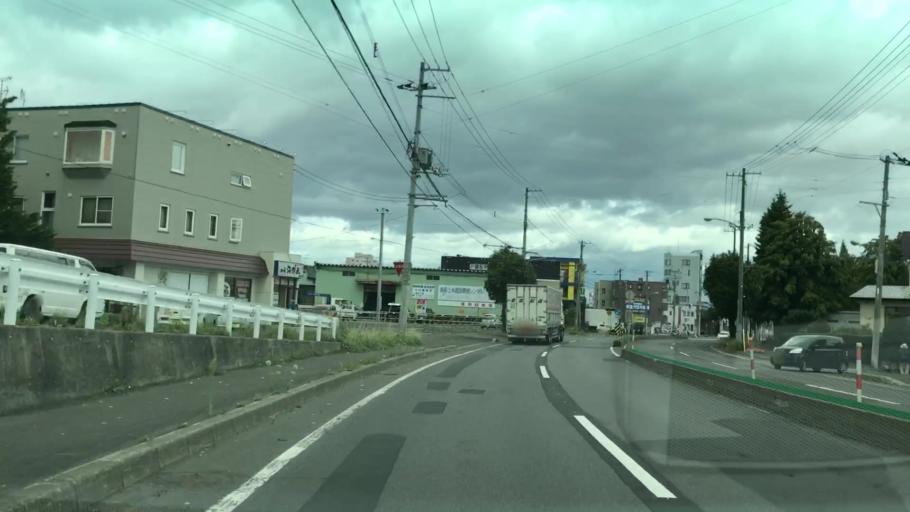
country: JP
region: Hokkaido
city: Sapporo
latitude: 42.9921
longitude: 141.4406
